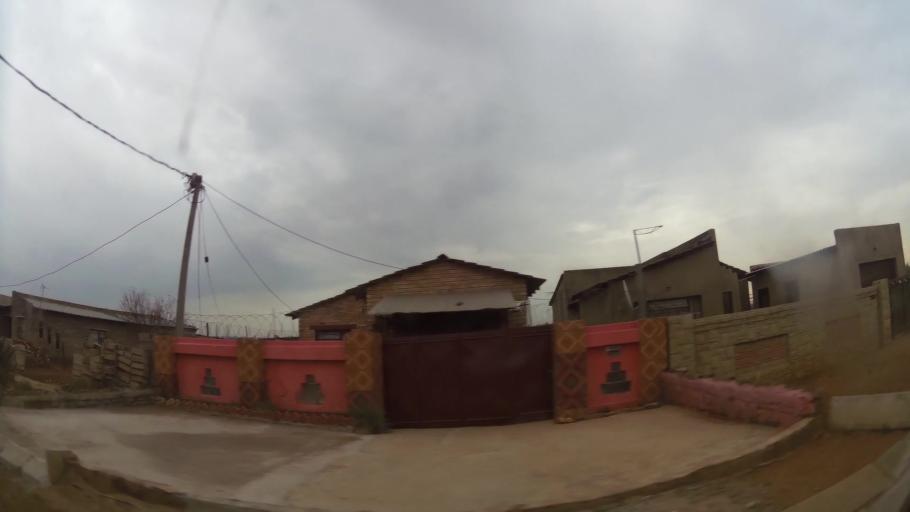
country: ZA
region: Gauteng
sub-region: Ekurhuleni Metropolitan Municipality
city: Germiston
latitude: -26.3817
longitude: 28.1728
